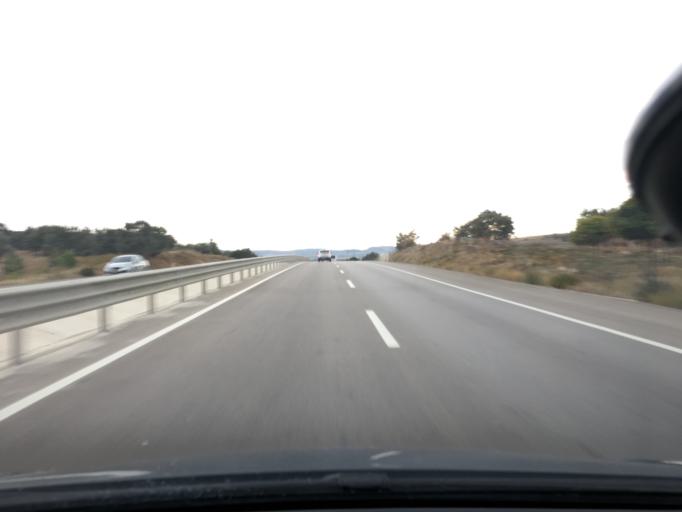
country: TR
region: Afyonkarahisar
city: Sincanli
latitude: 38.6487
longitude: 30.3140
